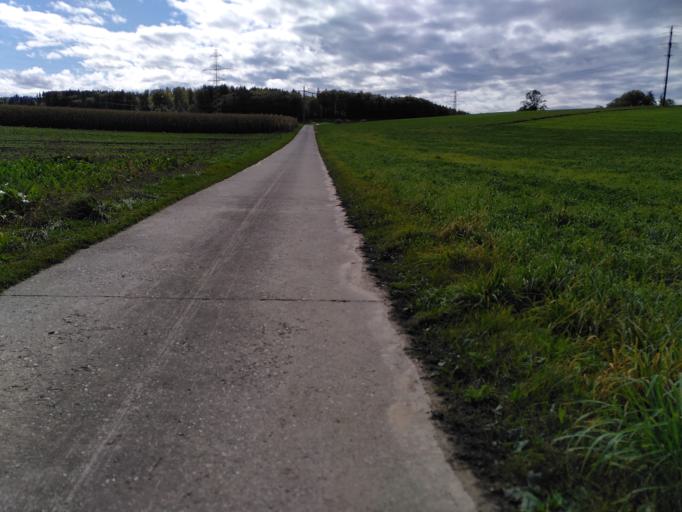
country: CH
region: Bern
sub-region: Emmental District
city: Koppigen
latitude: 47.1199
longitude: 7.6260
